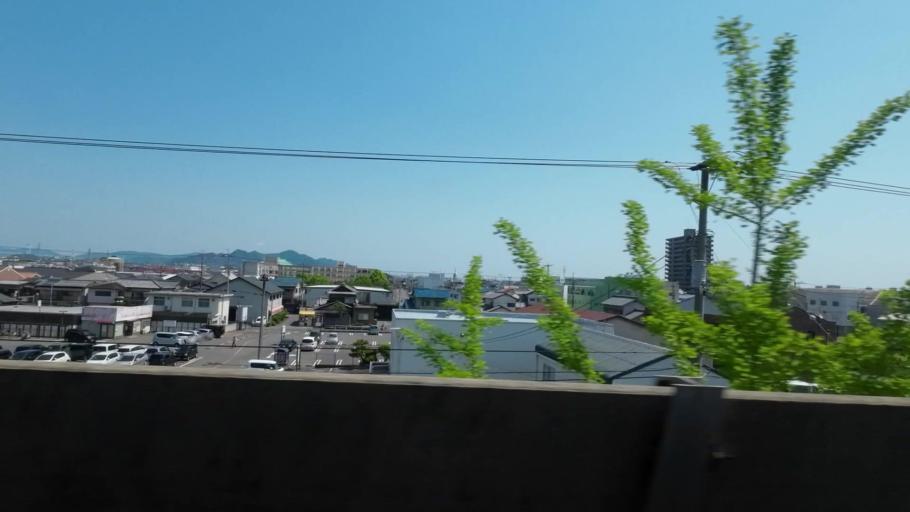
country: JP
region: Ehime
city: Hojo
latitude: 34.0686
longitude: 132.9896
